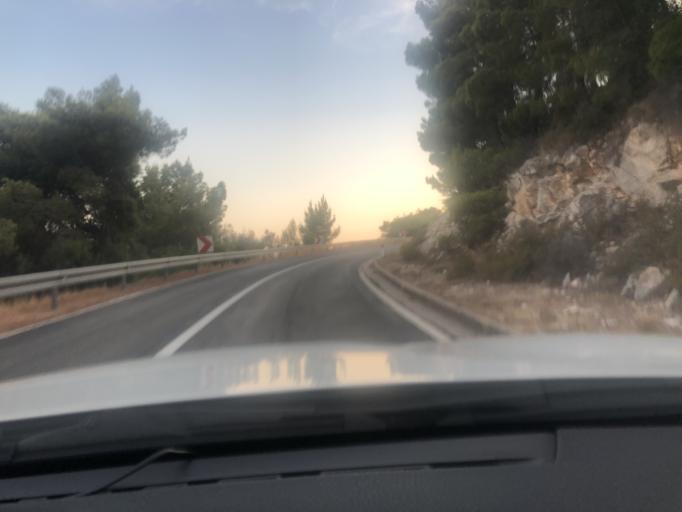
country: HR
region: Splitsko-Dalmatinska
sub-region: Grad Hvar
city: Hvar
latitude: 43.1645
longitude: 16.4866
